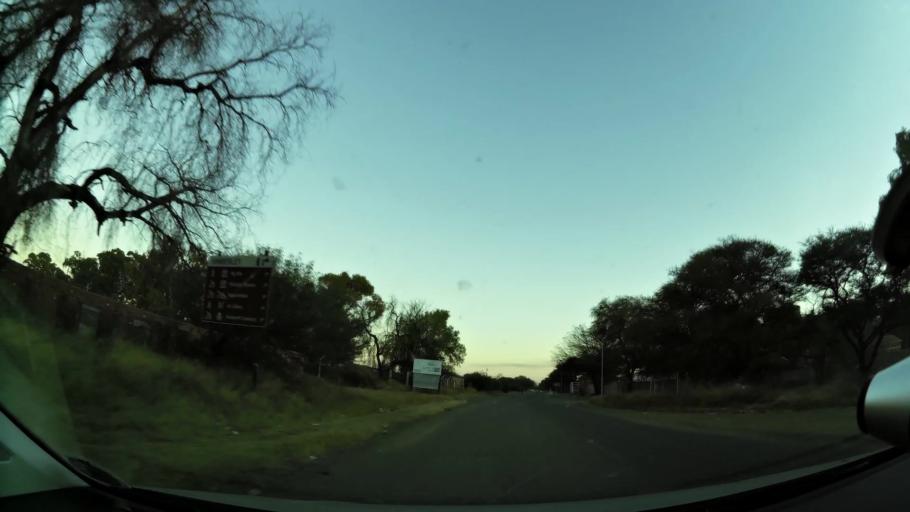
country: ZA
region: Northern Cape
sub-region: Frances Baard District Municipality
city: Kimberley
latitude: -28.7243
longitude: 24.7760
